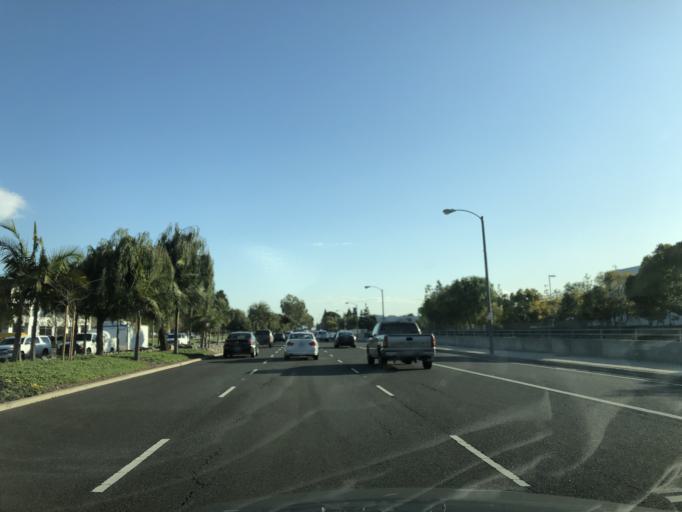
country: US
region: California
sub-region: Orange County
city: Cypress
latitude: 33.8020
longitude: -118.0285
